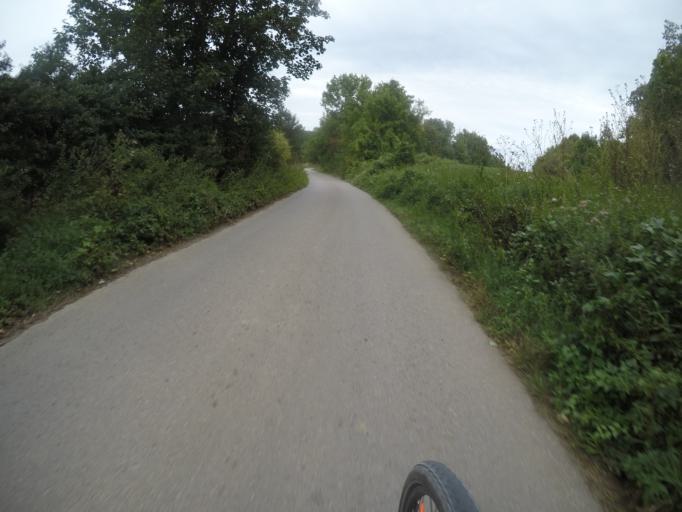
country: DE
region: Baden-Wuerttemberg
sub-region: Regierungsbezirk Stuttgart
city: Oberriexingen
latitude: 48.9289
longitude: 9.0389
